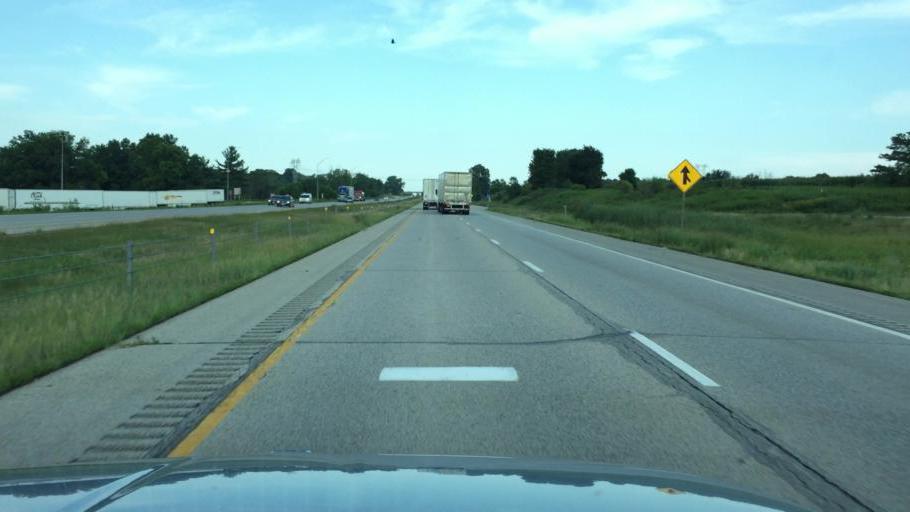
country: US
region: Iowa
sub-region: Johnson County
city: Tiffin
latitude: 41.6943
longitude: -91.6819
